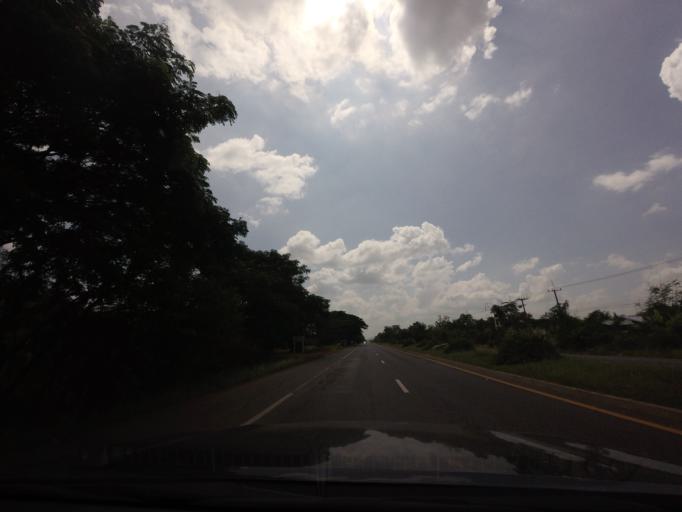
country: TH
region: Phetchabun
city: Nong Phai
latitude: 16.1564
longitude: 101.0658
